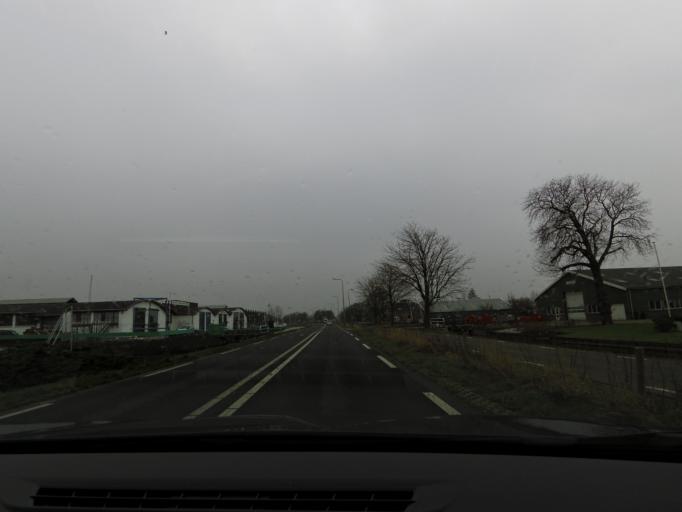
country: NL
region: South Holland
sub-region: Gemeente Nieuwkoop
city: Nieuwkoop
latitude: 52.1613
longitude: 4.7790
